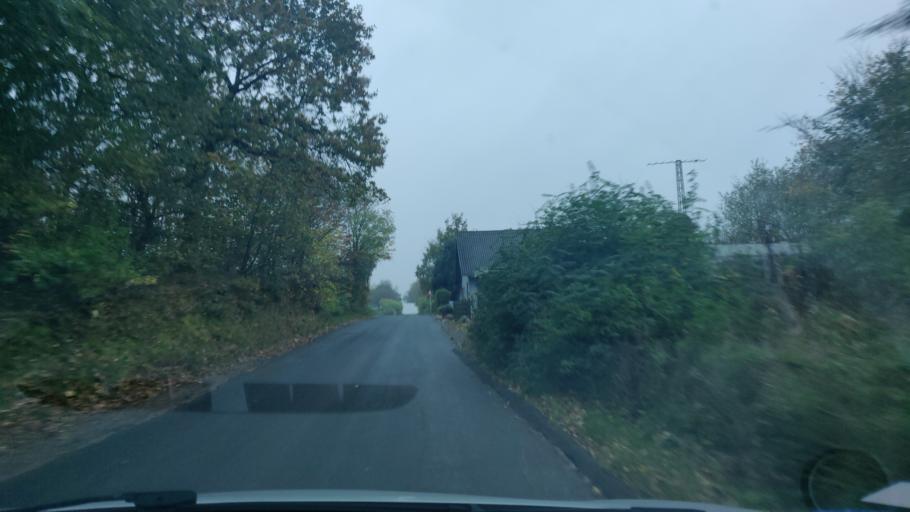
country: DK
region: South Denmark
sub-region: Kolding Kommune
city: Kolding
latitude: 55.5655
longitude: 9.4174
